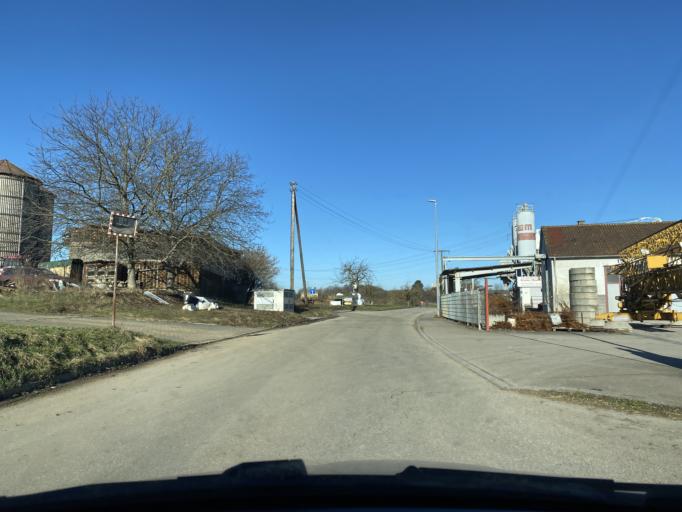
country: DE
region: Baden-Wuerttemberg
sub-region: Regierungsbezirk Stuttgart
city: Eberdingen
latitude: 48.8981
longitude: 8.9322
